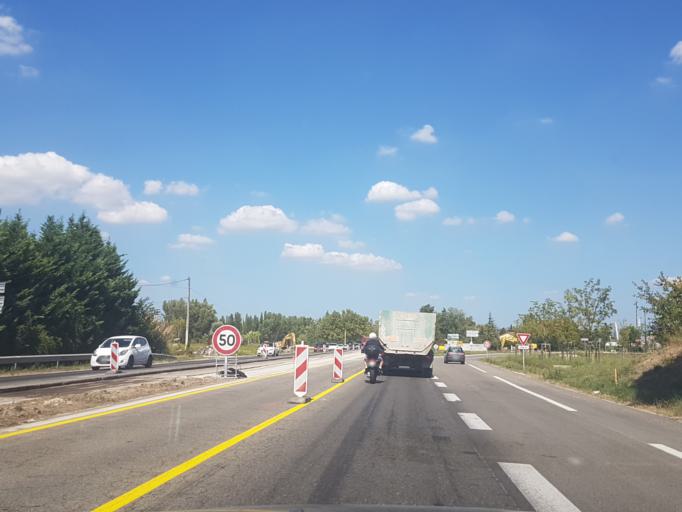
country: FR
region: Provence-Alpes-Cote d'Azur
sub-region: Departement du Vaucluse
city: Althen-des-Paluds
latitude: 44.0166
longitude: 4.9604
